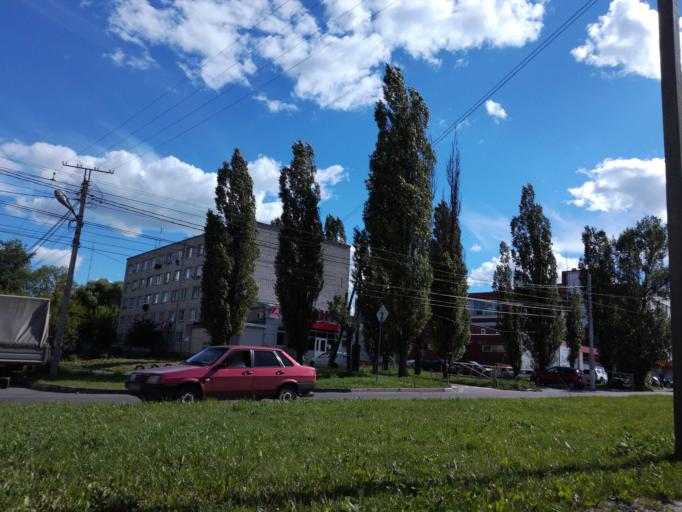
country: RU
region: Kursk
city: Kursk
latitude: 51.7553
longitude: 36.1398
